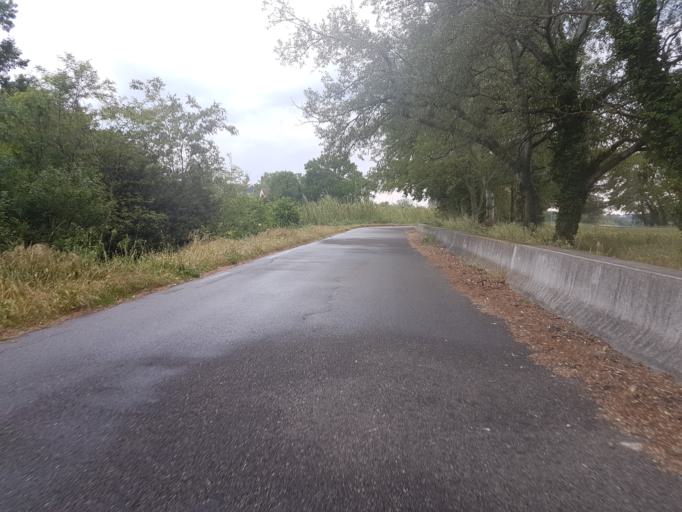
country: FR
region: Provence-Alpes-Cote d'Azur
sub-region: Departement du Vaucluse
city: Avignon
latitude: 43.9615
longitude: 4.8134
